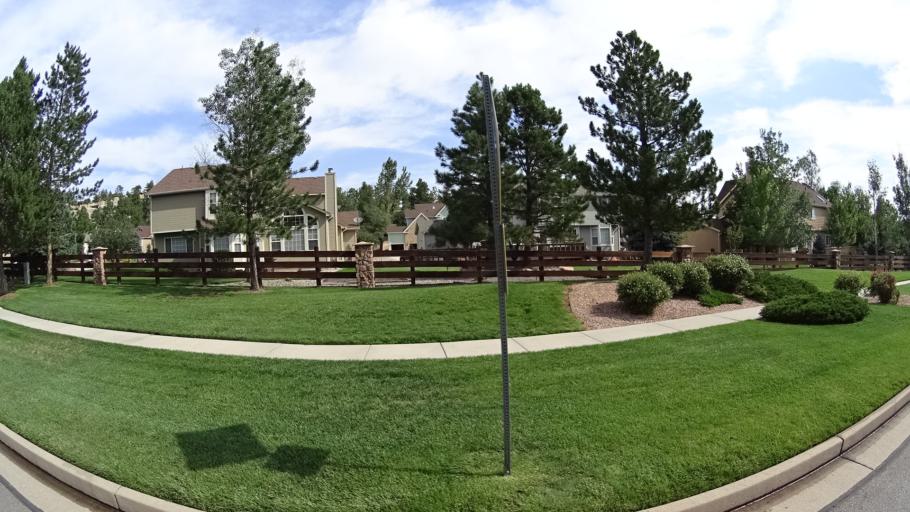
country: US
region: Colorado
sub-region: El Paso County
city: Air Force Academy
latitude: 38.9425
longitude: -104.8607
